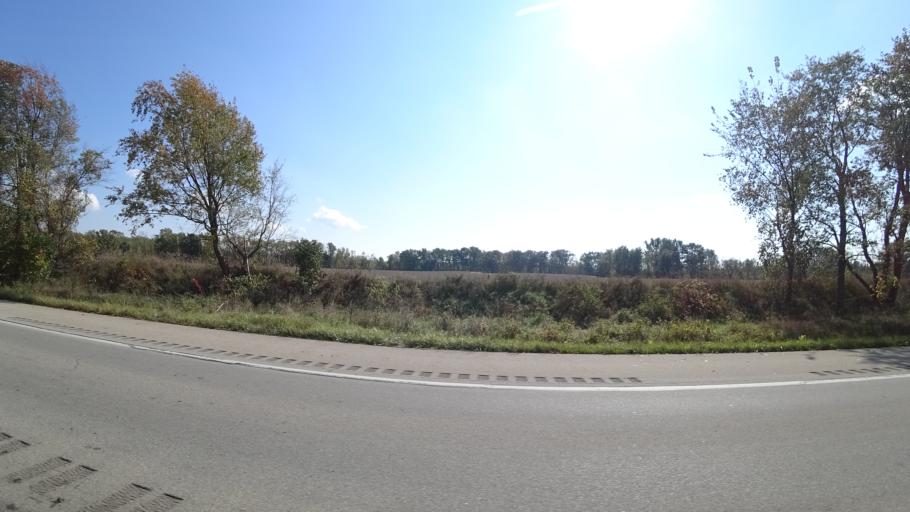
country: US
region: Michigan
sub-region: Calhoun County
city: Homer
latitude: 42.1476
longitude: -84.8220
